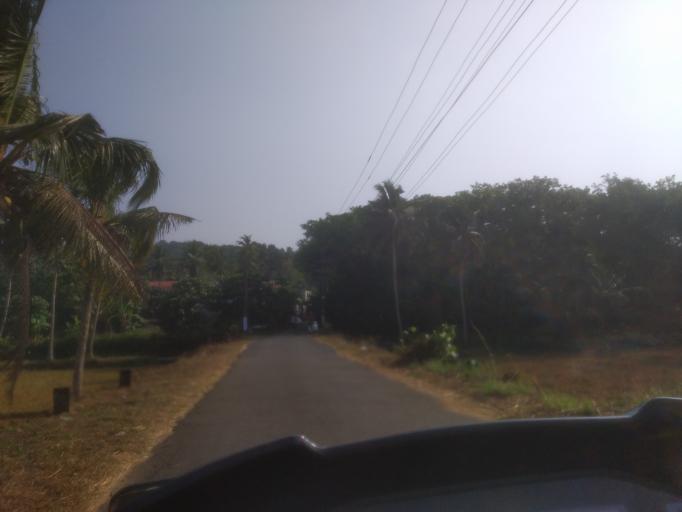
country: IN
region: Kerala
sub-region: Ernakulam
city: Piravam
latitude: 9.8401
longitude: 76.5250
